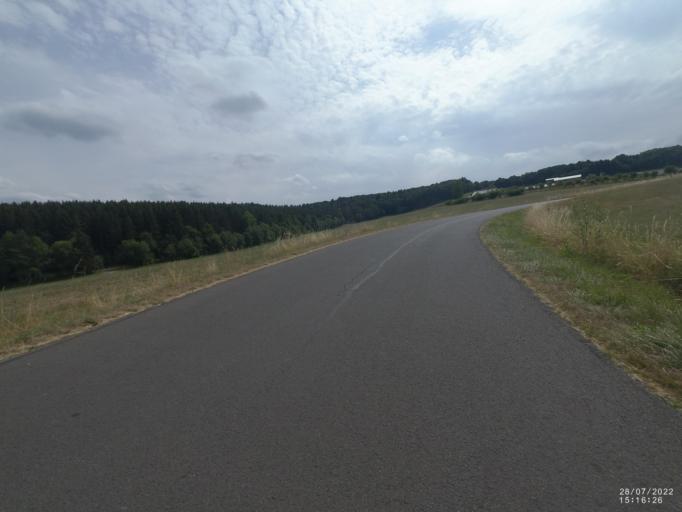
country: DE
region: Rheinland-Pfalz
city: Oberbettingen
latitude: 50.2656
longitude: 6.6432
